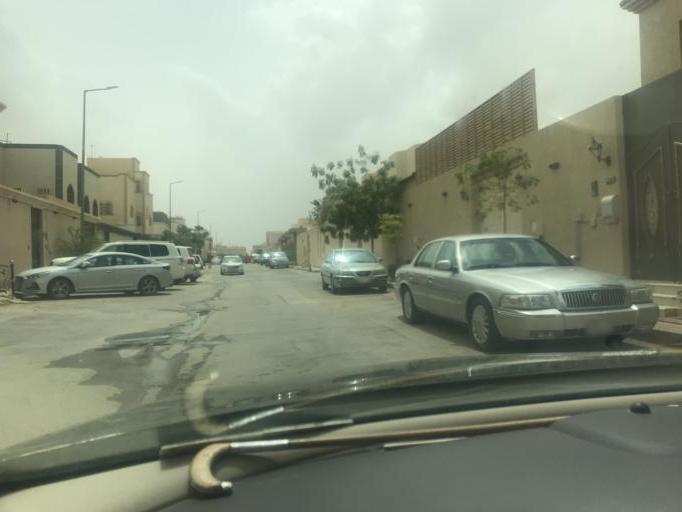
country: SA
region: Ar Riyad
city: Riyadh
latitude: 24.7352
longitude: 46.7875
